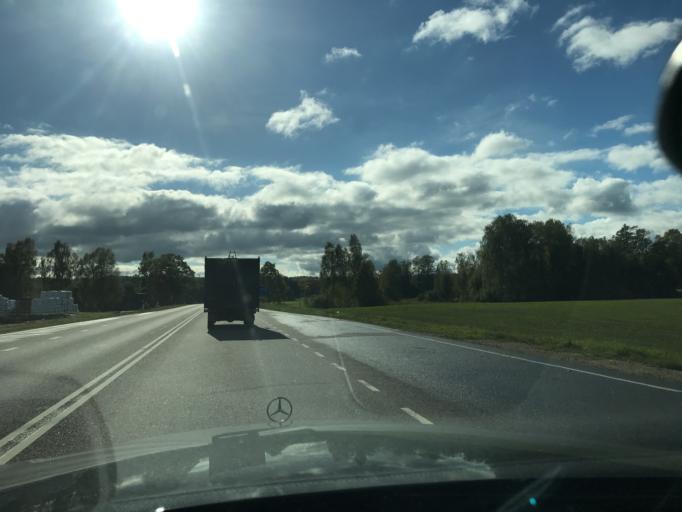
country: EE
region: Vorumaa
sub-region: Voru linn
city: Voru
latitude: 57.8147
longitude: 27.0648
